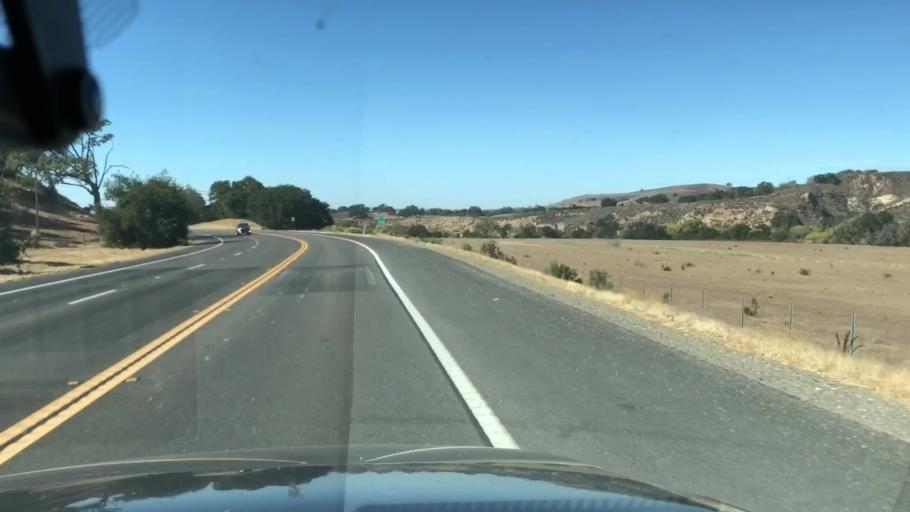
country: US
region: California
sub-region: Santa Barbara County
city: Santa Ynez
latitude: 34.5879
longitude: -120.0151
